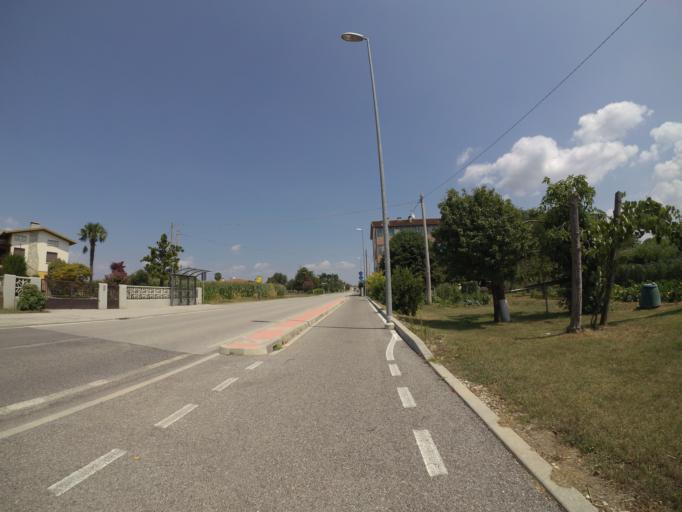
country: IT
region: Friuli Venezia Giulia
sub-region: Provincia di Udine
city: Sedegliano
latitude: 46.0077
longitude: 12.9684
